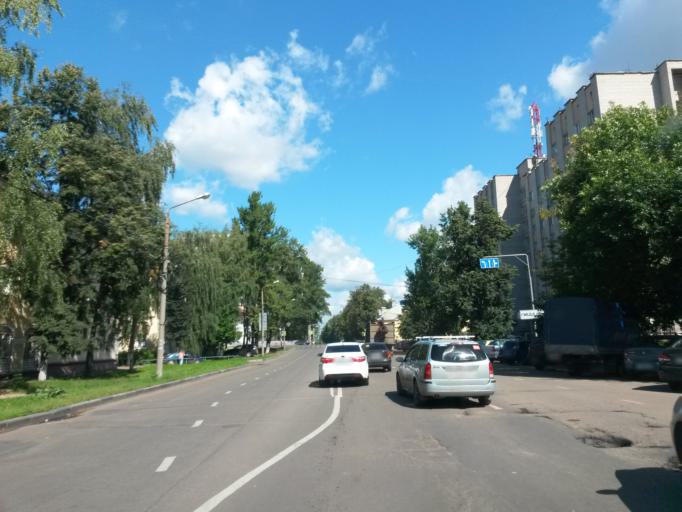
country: RU
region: Jaroslavl
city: Yaroslavl
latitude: 57.5977
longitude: 39.8784
